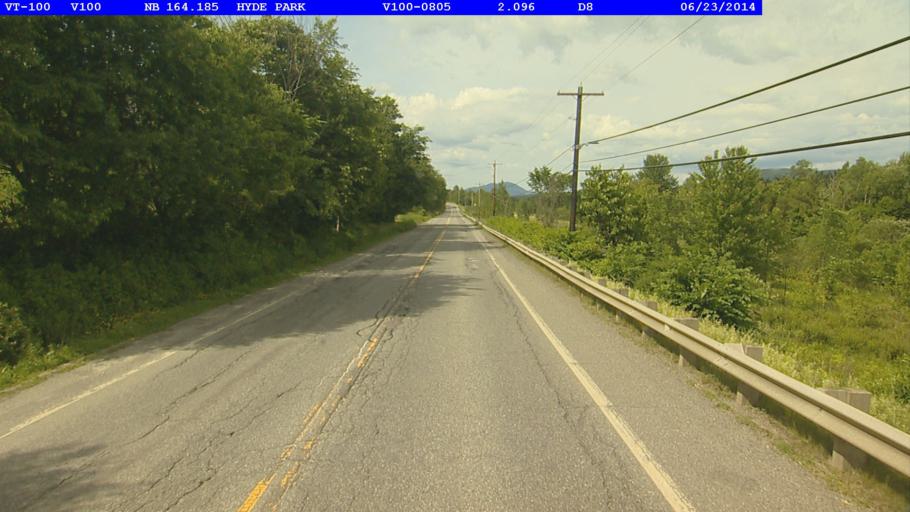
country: US
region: Vermont
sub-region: Lamoille County
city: Hyde Park
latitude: 44.6250
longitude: -72.5994
